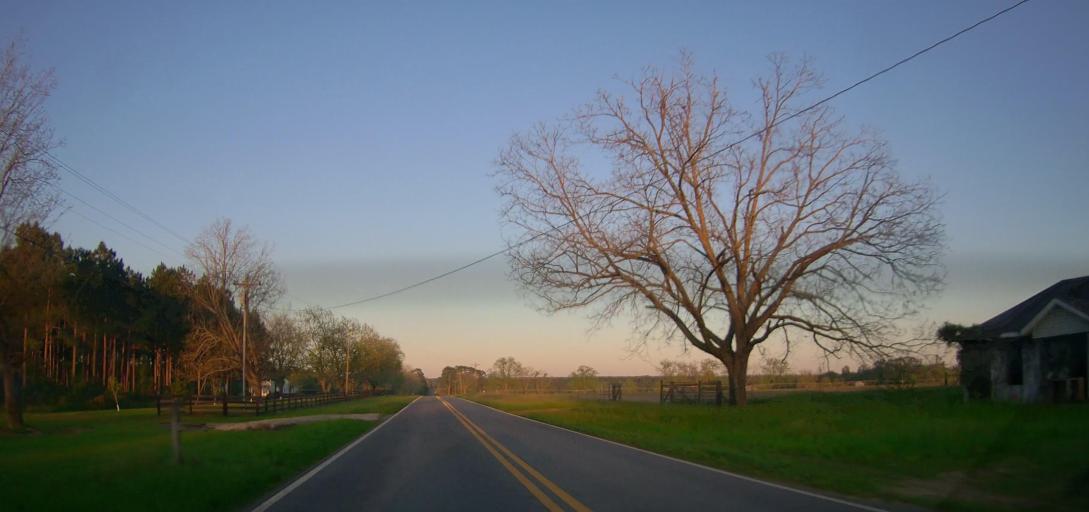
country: US
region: Georgia
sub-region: Ben Hill County
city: Fitzgerald
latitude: 31.7180
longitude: -83.3072
